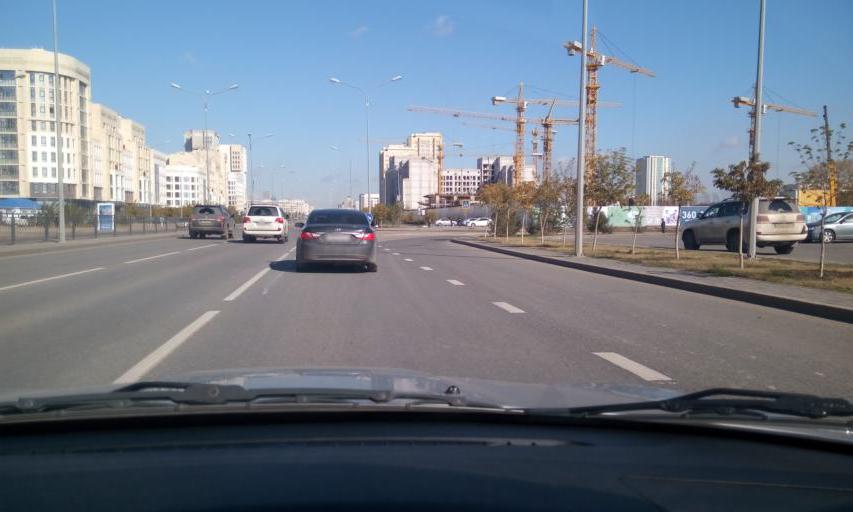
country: KZ
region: Astana Qalasy
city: Astana
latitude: 51.0904
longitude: 71.4252
